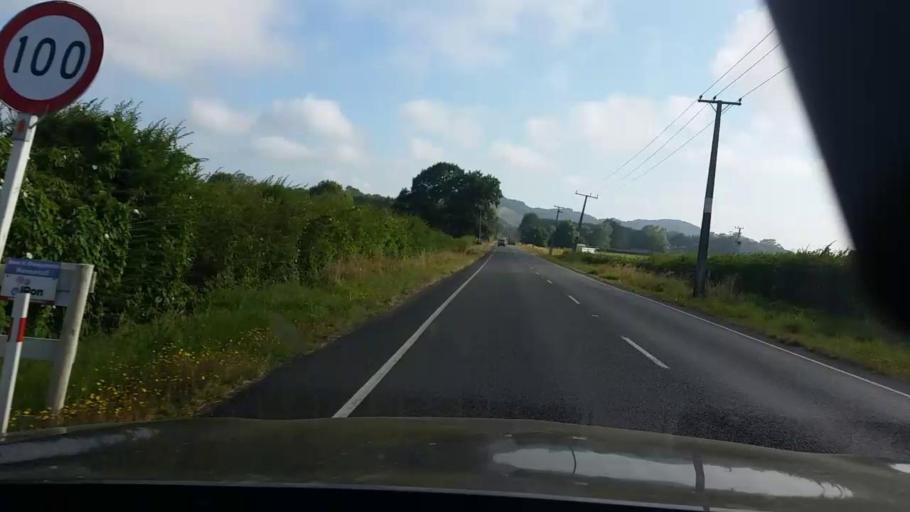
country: NZ
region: Waikato
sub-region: Hamilton City
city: Hamilton
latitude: -37.6093
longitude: 175.3473
